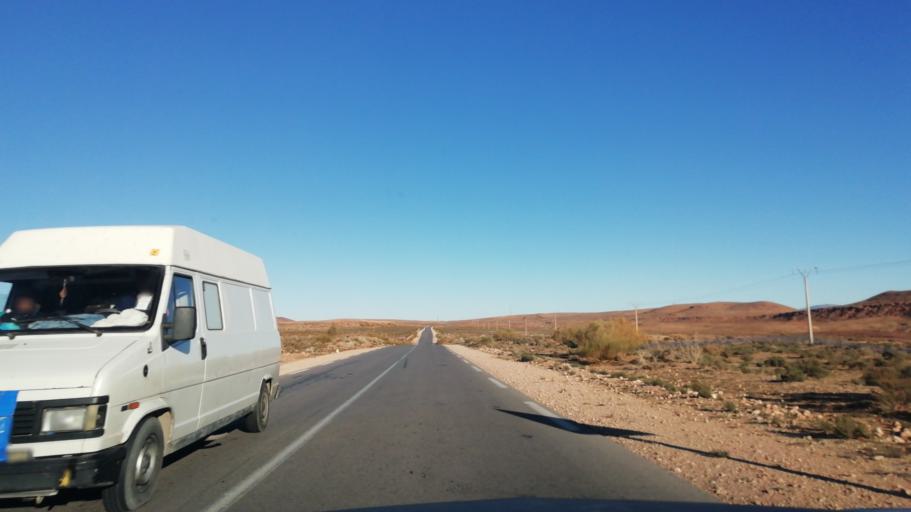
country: DZ
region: El Bayadh
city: El Abiodh Sidi Cheikh
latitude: 33.1651
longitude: 0.4138
